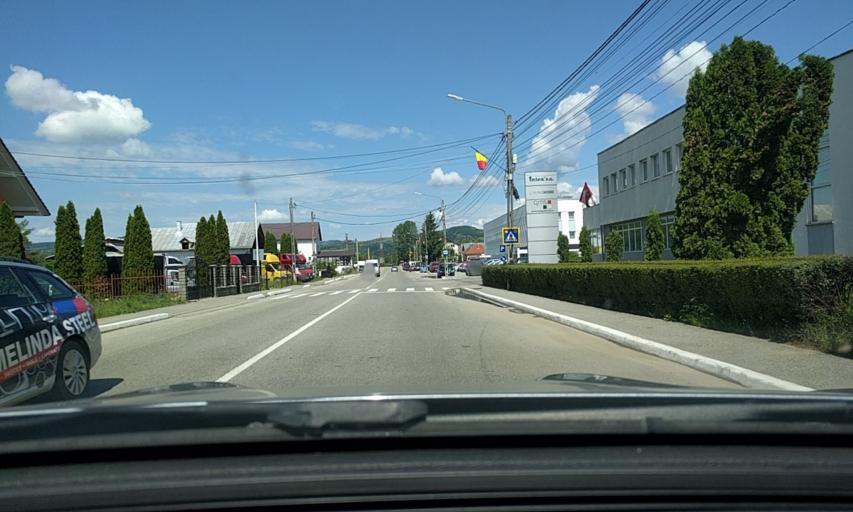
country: RO
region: Bistrita-Nasaud
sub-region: Oras Nasaud
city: Nasaud
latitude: 47.2950
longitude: 24.3831
